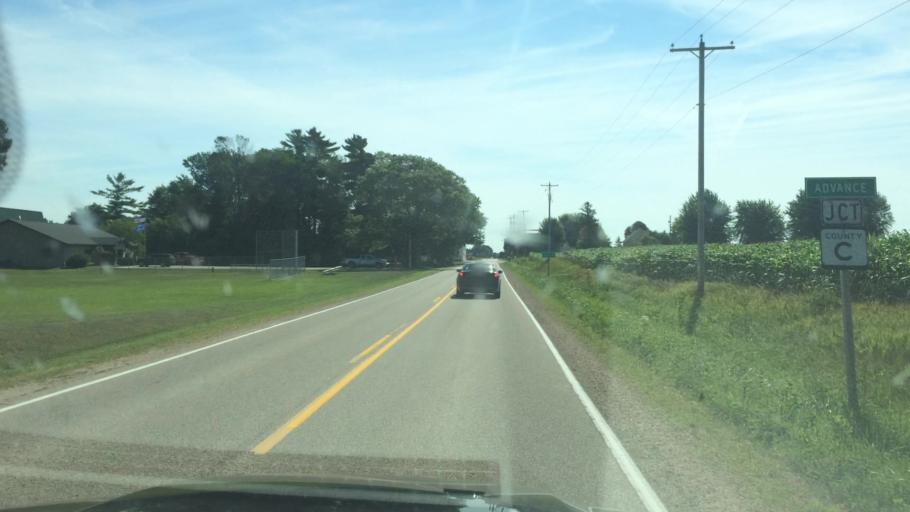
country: US
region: Wisconsin
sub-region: Oconto County
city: Gillett
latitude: 44.7874
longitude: -88.3358
